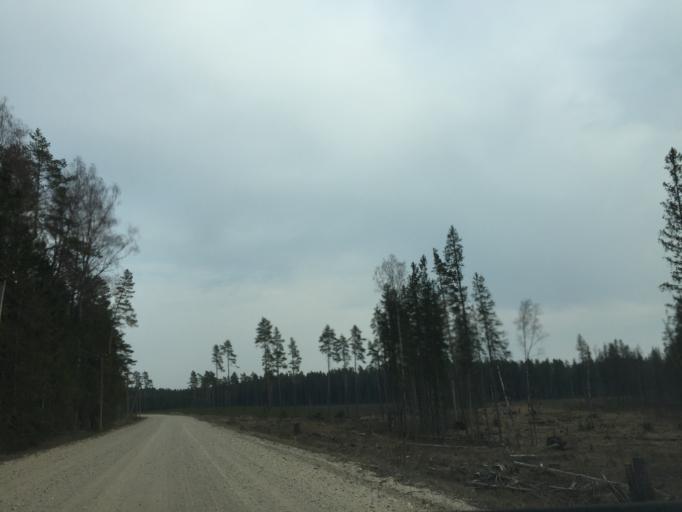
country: LV
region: Raunas
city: Rauna
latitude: 57.1583
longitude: 25.5354
